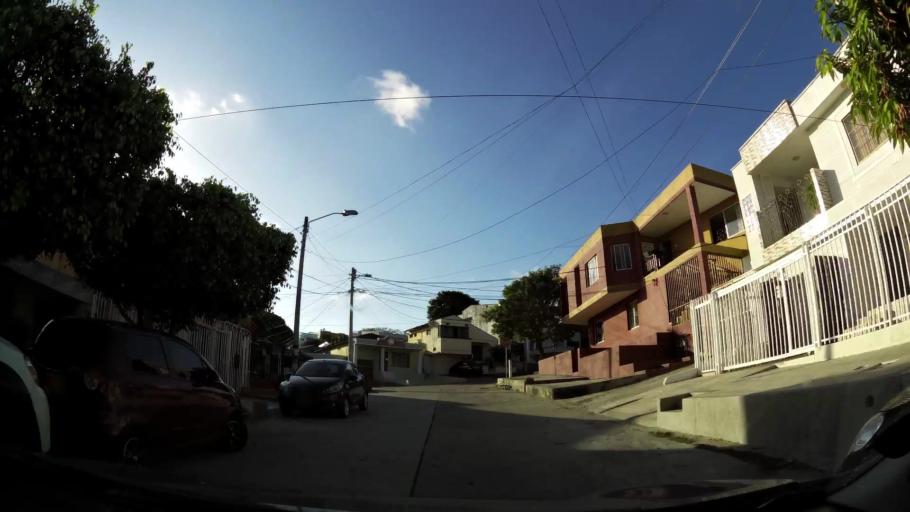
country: CO
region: Atlantico
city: Barranquilla
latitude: 10.9824
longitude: -74.8063
